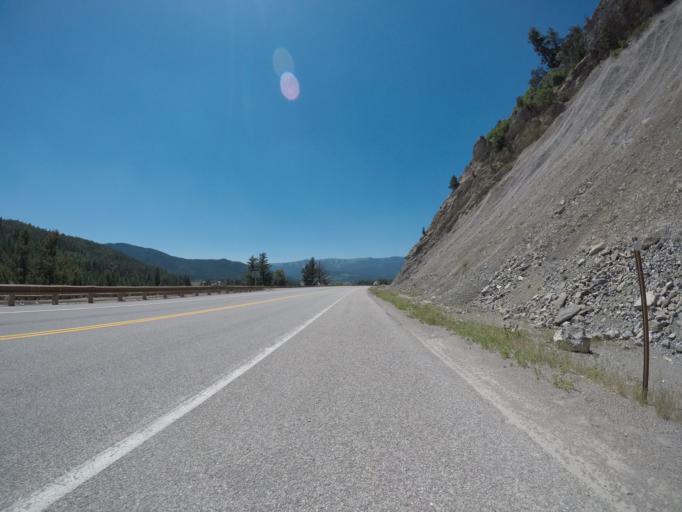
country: US
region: Wyoming
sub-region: Teton County
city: Hoback
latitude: 43.1763
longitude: -110.9999
